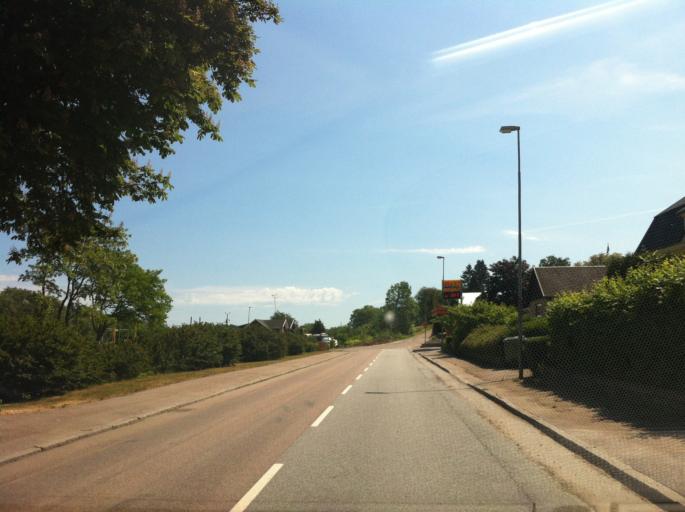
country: SE
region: Skane
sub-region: Helsingborg
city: Glumslov
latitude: 55.9610
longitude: 12.8416
